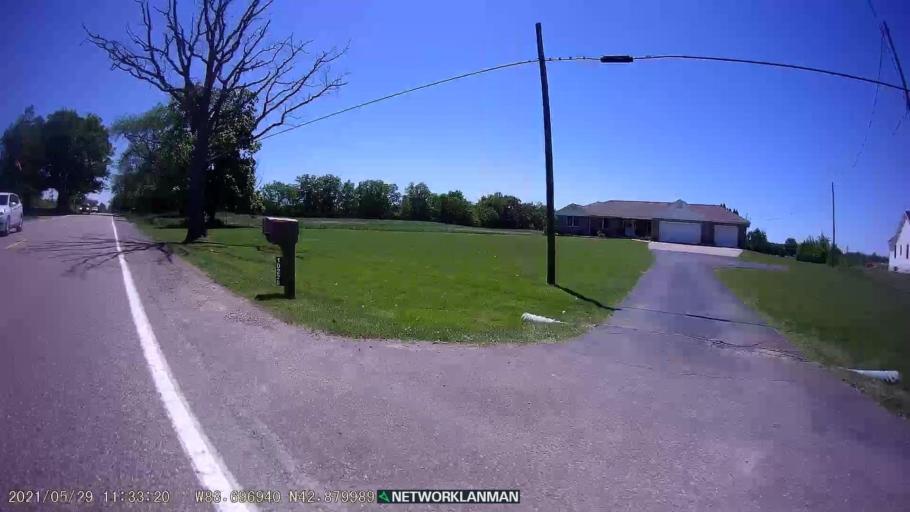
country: US
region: Michigan
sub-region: Genesee County
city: Lake Fenton
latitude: 42.8798
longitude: -83.6970
